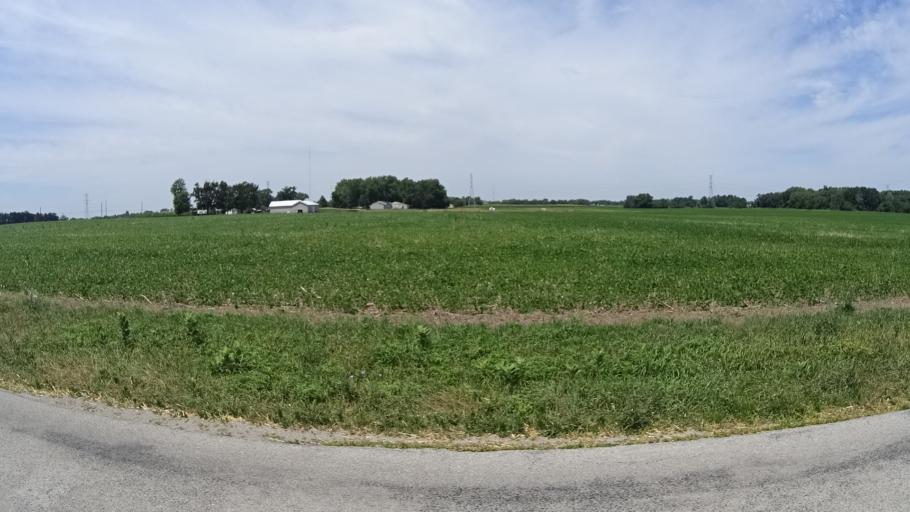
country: US
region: Ohio
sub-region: Erie County
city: Sandusky
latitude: 41.3799
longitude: -82.7851
